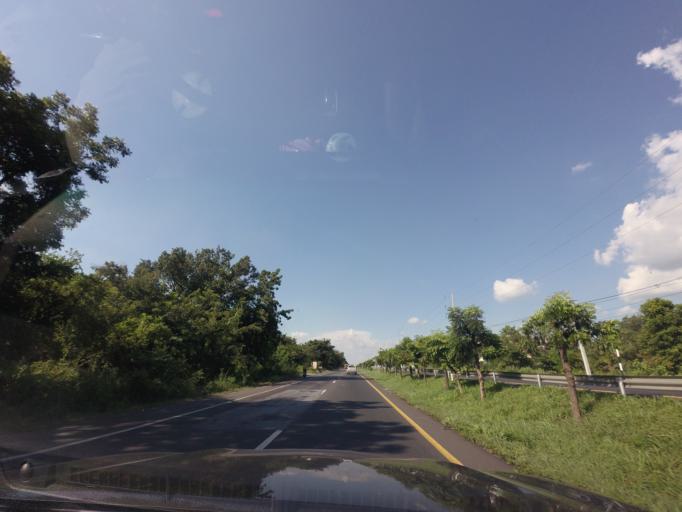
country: TH
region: Nakhon Ratchasima
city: Sida
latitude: 15.5555
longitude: 102.5500
